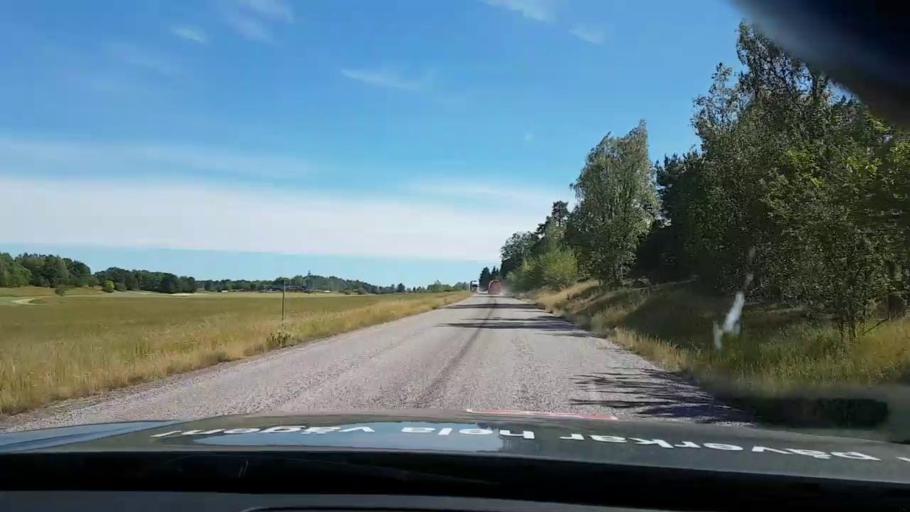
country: SE
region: Kalmar
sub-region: Vasterviks Kommun
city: Forserum
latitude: 57.9466
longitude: 16.4482
